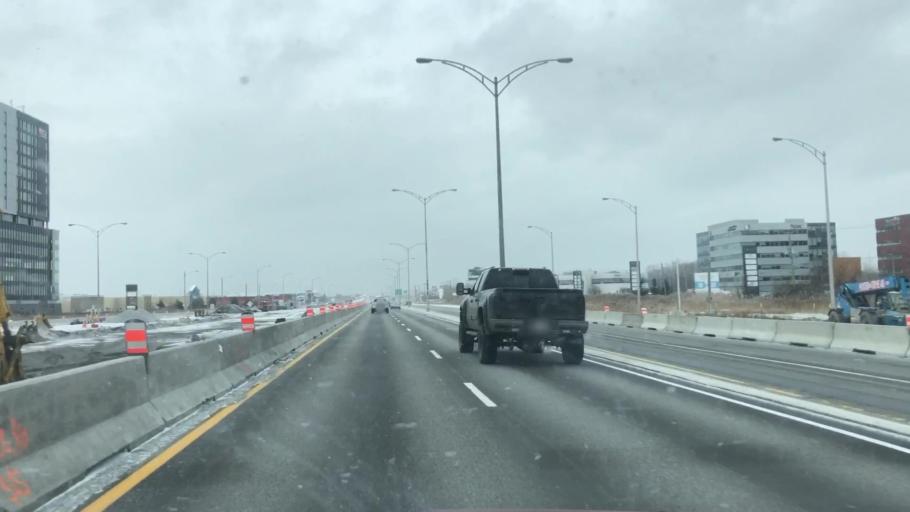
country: CA
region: Quebec
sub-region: Monteregie
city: Brossard
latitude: 45.4473
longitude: -73.4340
